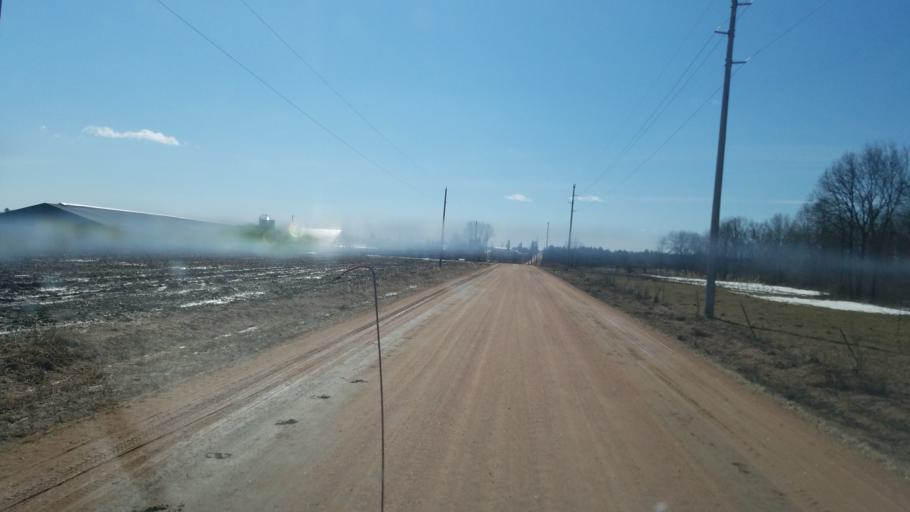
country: US
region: Wisconsin
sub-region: Clark County
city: Loyal
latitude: 44.5950
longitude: -90.3962
